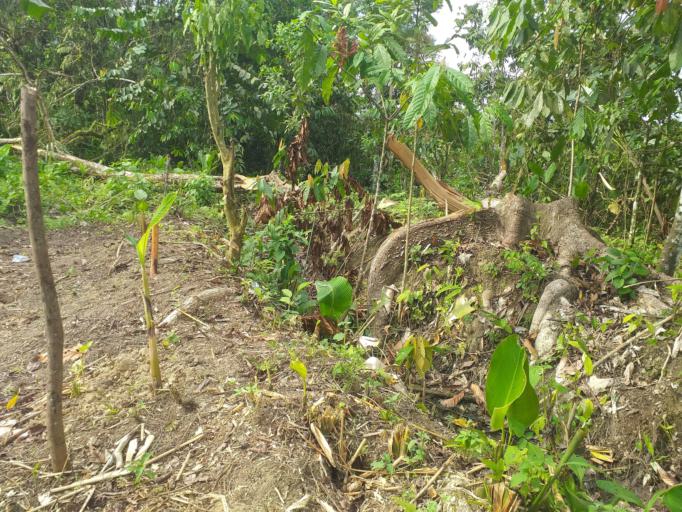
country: CO
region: Narino
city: La Tola
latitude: 2.3393
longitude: -78.3238
